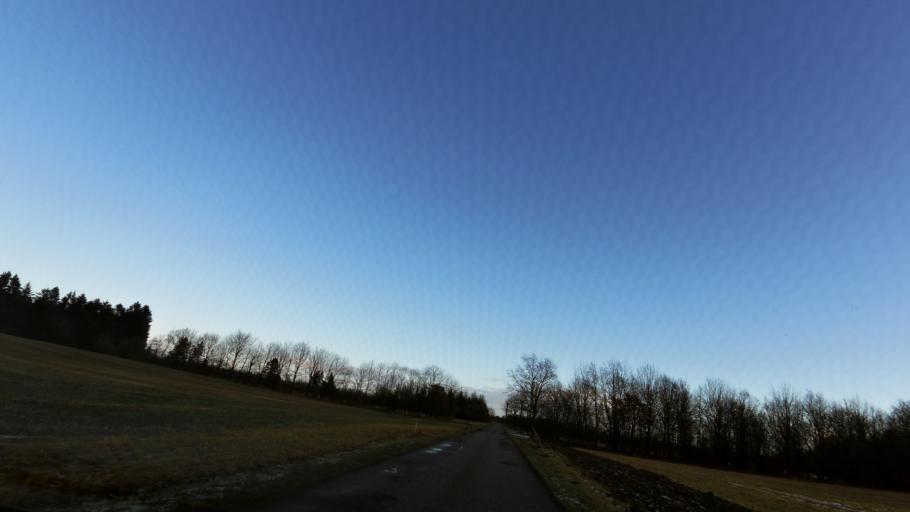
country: DK
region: Central Jutland
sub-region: Ikast-Brande Kommune
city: Ikast
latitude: 56.0278
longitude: 9.2259
